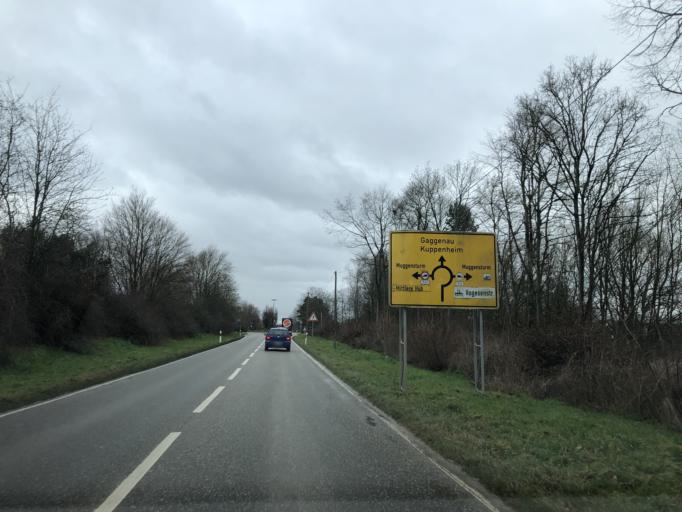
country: DE
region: Baden-Wuerttemberg
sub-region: Karlsruhe Region
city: Muggensturm
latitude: 48.8774
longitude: 8.2926
